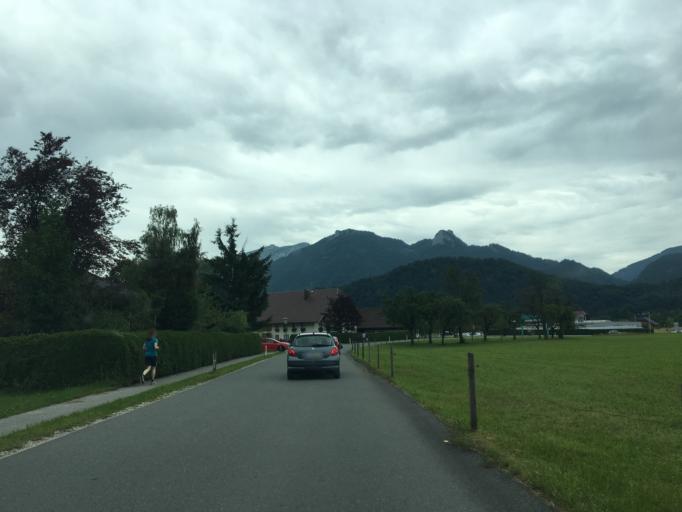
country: AT
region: Salzburg
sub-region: Politischer Bezirk Salzburg-Umgebung
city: Strobl
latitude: 47.7100
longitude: 13.4889
